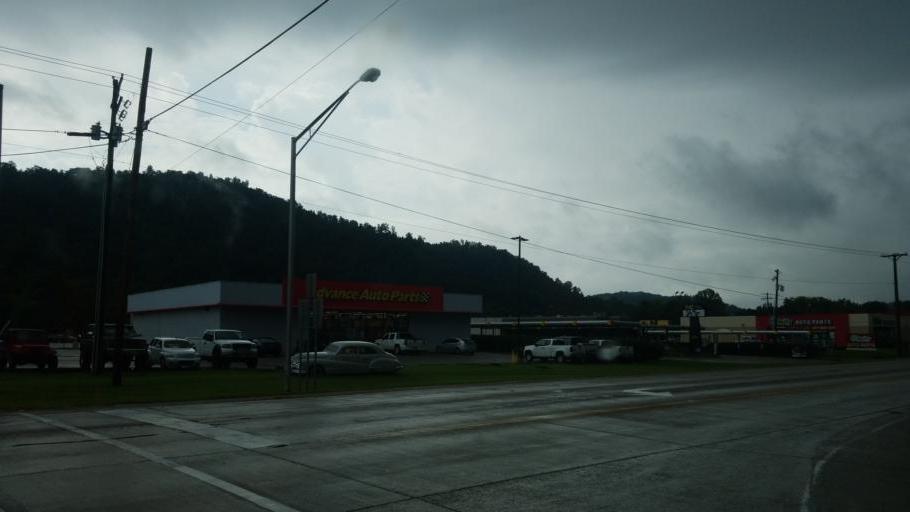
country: US
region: Kentucky
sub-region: Rowan County
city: Morehead
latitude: 38.1768
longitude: -83.4359
